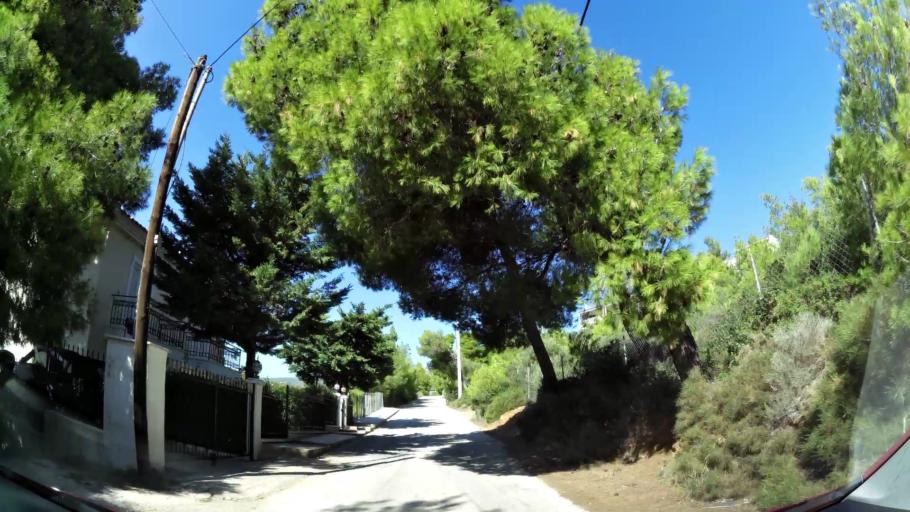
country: GR
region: Attica
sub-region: Nomarchia Anatolikis Attikis
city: Dioni
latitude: 38.0286
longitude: 23.9347
